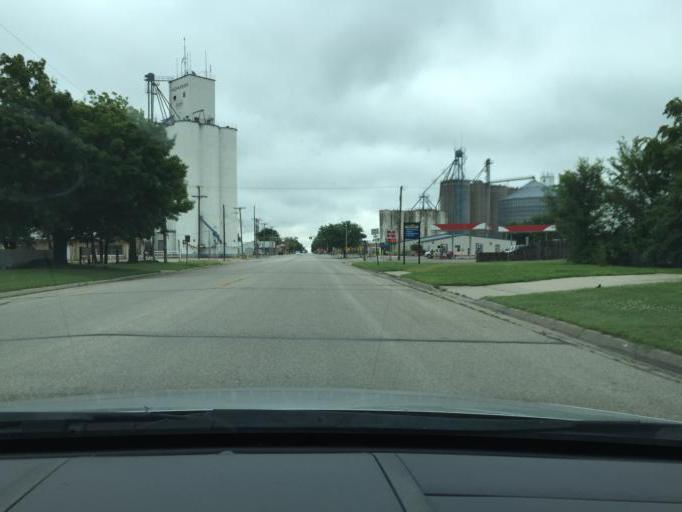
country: US
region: Kansas
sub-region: McPherson County
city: Moundridge
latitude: 38.2030
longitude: -97.5246
